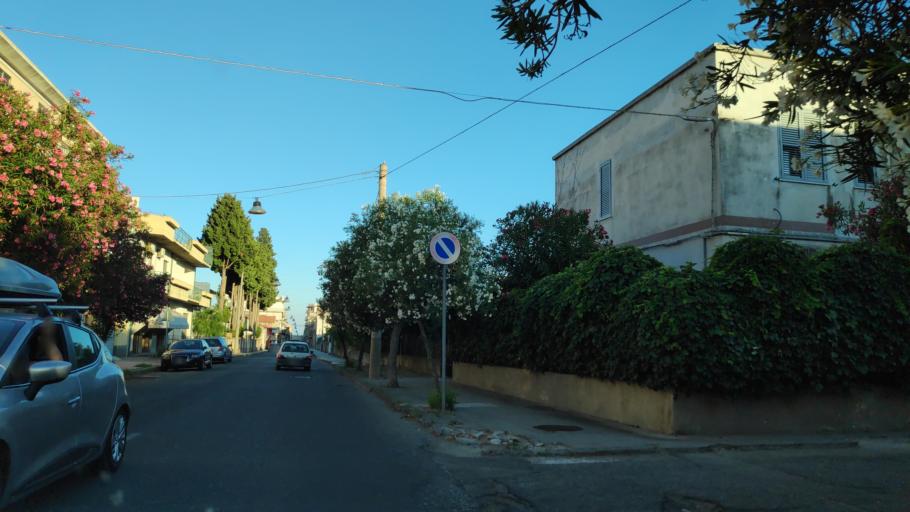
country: IT
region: Calabria
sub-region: Provincia di Reggio Calabria
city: Locri
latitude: 38.2366
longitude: 16.2592
